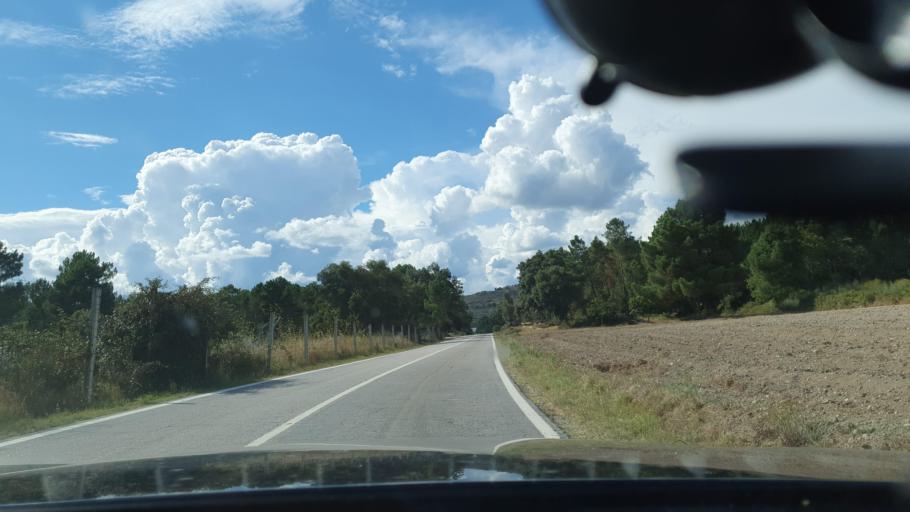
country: PT
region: Vila Real
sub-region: Chaves
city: Chaves
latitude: 41.7103
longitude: -7.5541
